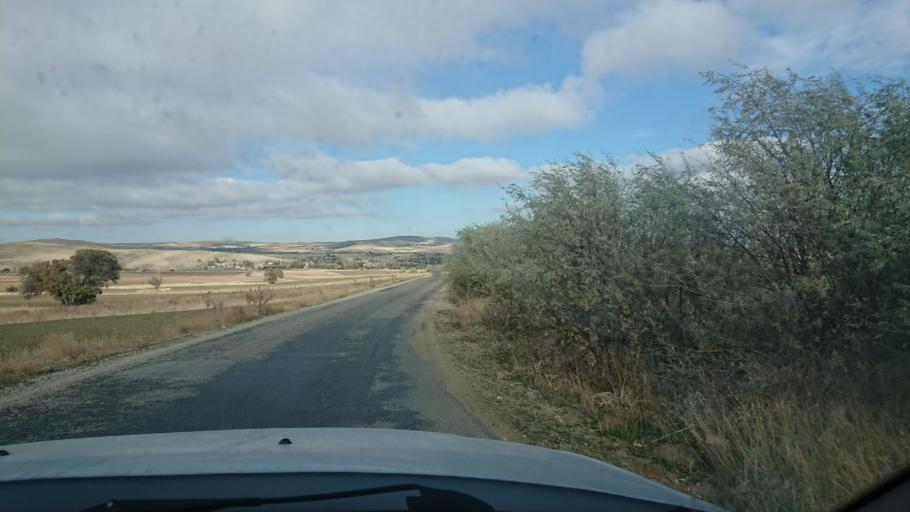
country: TR
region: Aksaray
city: Ortakoy
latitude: 38.7958
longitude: 33.9944
